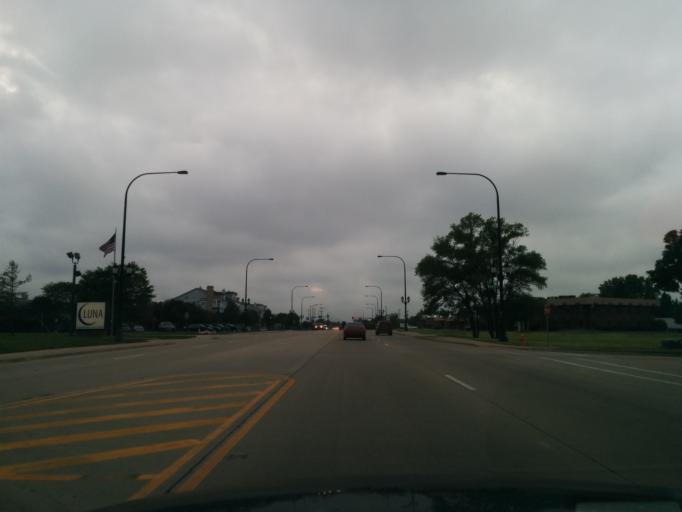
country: US
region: Illinois
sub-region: DuPage County
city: Addison
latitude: 41.9433
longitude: -88.0148
